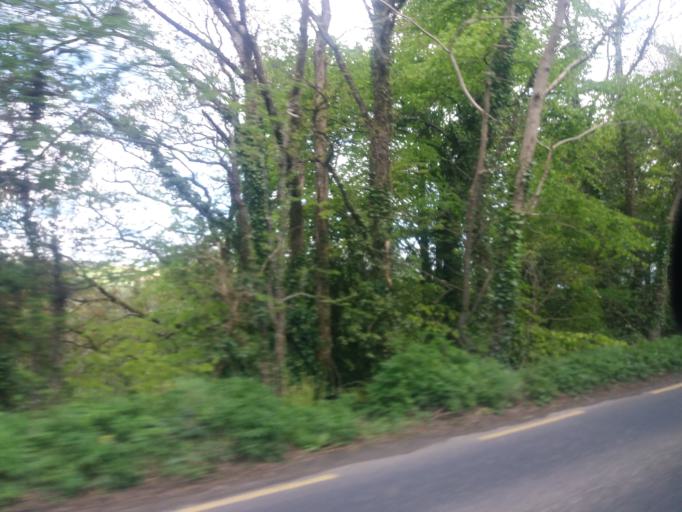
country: IE
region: Leinster
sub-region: Loch Garman
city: New Ross
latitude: 52.2690
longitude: -6.7420
